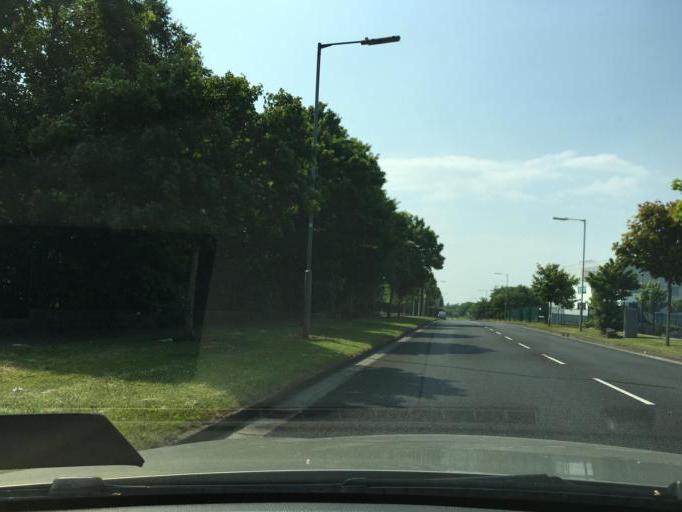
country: IE
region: Leinster
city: Hartstown
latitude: 53.4083
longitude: -6.4050
